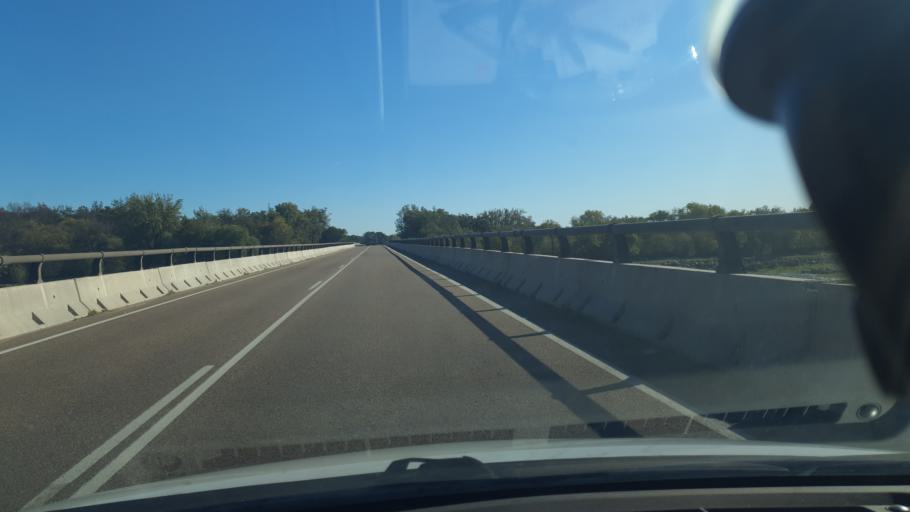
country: ES
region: Castille and Leon
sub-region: Provincia de Avila
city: Candeleda
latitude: 40.1393
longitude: -5.2530
